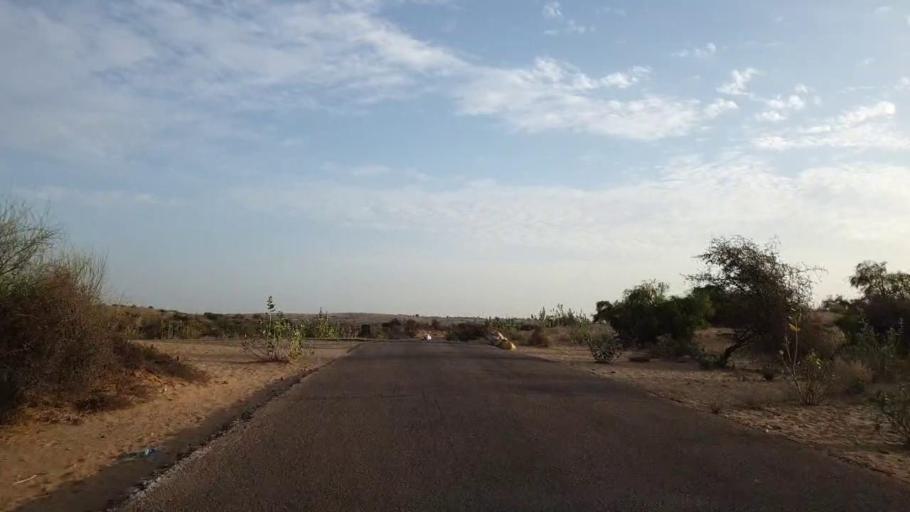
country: PK
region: Sindh
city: Nabisar
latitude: 25.0975
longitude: 69.9928
